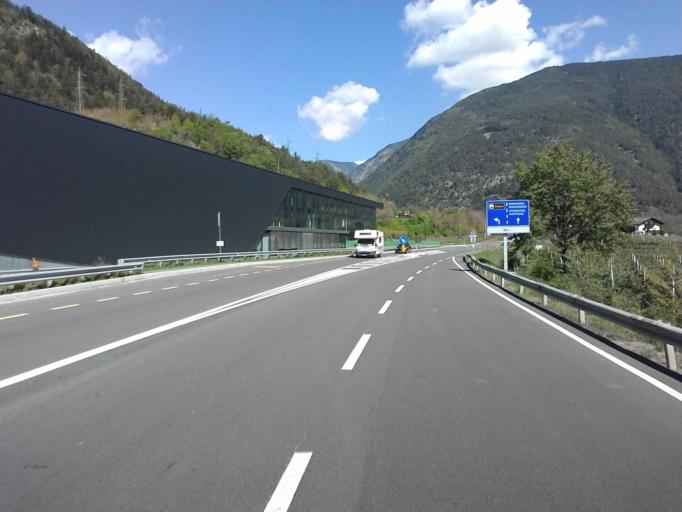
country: IT
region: Trentino-Alto Adige
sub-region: Bolzano
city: Naz-Sciaves - Natz-Schabs
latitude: 46.7678
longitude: 11.6400
